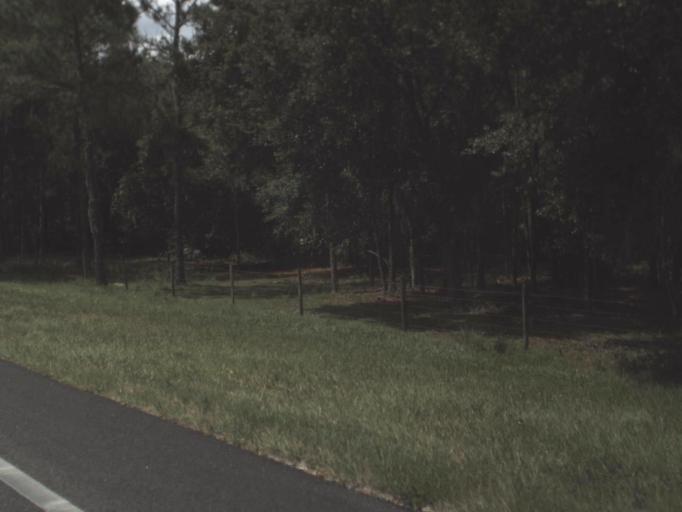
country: US
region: Florida
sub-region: Polk County
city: Alturas
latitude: 27.9054
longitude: -81.6666
